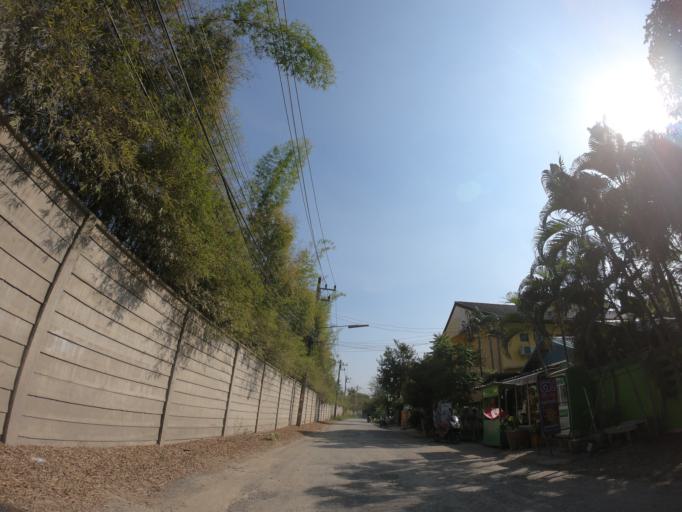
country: TH
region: Chiang Mai
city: Chiang Mai
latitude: 18.8248
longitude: 98.9848
